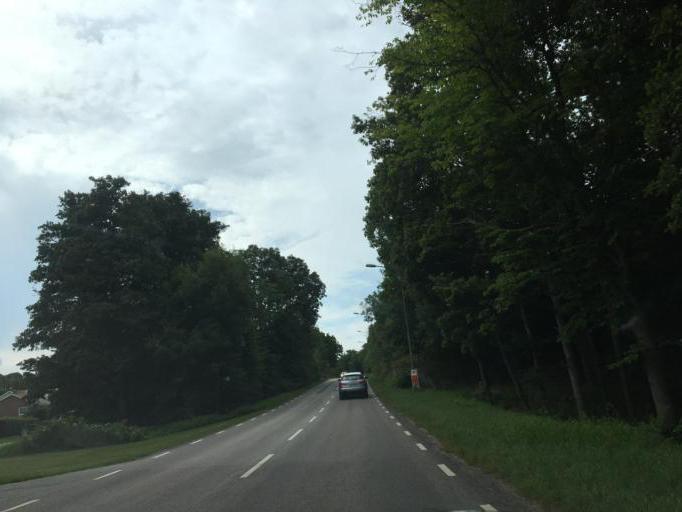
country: SE
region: Vaestra Goetaland
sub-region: Sotenas Kommun
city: Hunnebostrand
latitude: 58.4312
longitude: 11.2984
